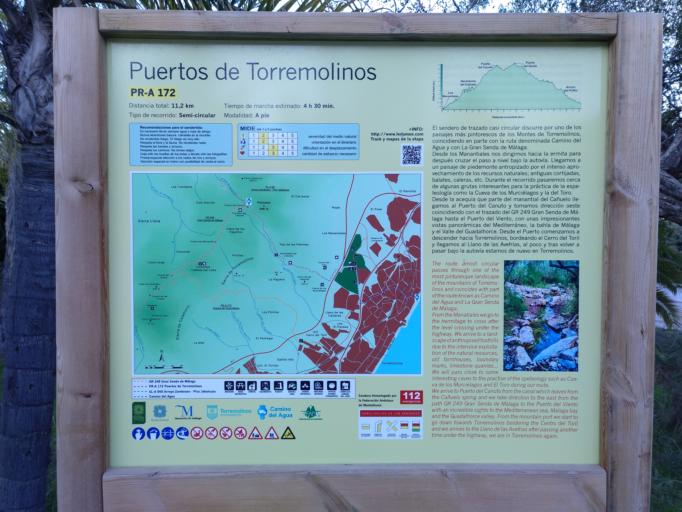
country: ES
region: Andalusia
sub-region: Provincia de Malaga
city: Torremolinos
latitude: 36.6287
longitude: -4.5106
